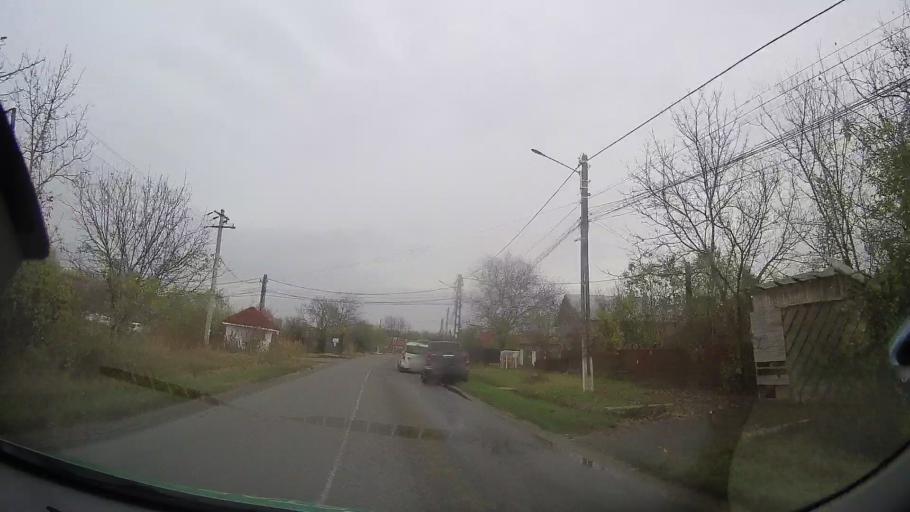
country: RO
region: Ilfov
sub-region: Comuna Gruiu
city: Gruiu
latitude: 44.7225
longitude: 26.2129
